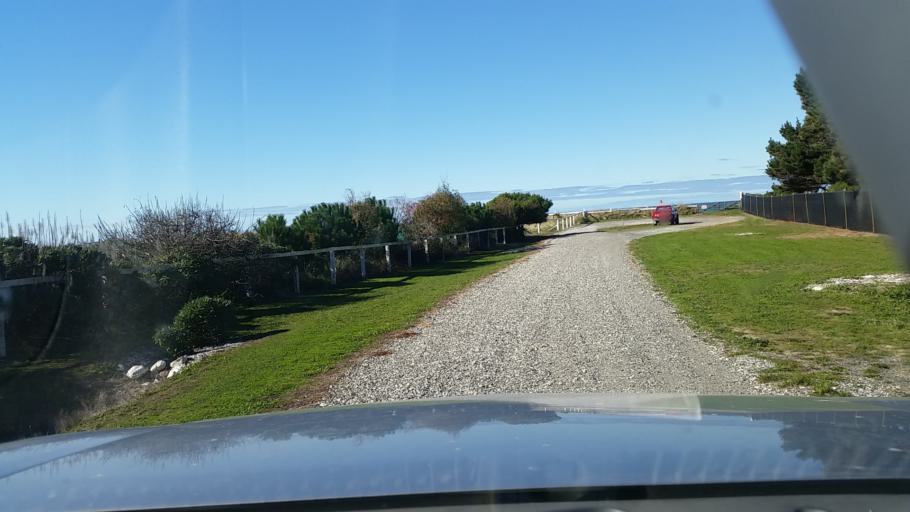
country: NZ
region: Marlborough
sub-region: Marlborough District
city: Blenheim
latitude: -41.6648
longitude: 174.1572
